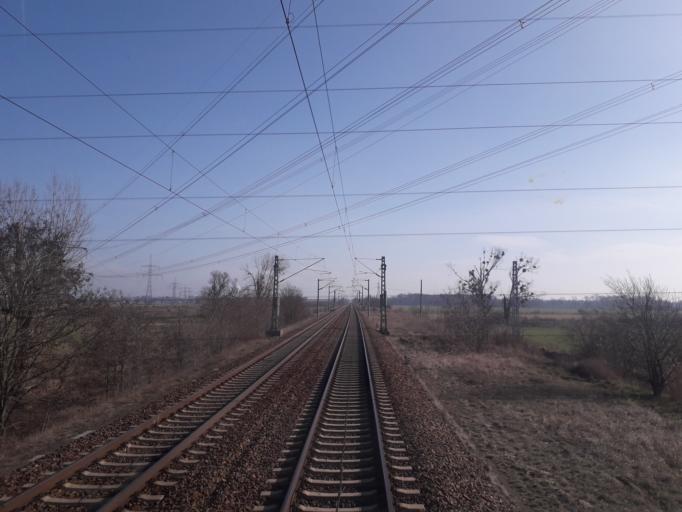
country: DE
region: Brandenburg
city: Wustermark
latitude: 52.6005
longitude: 12.9323
